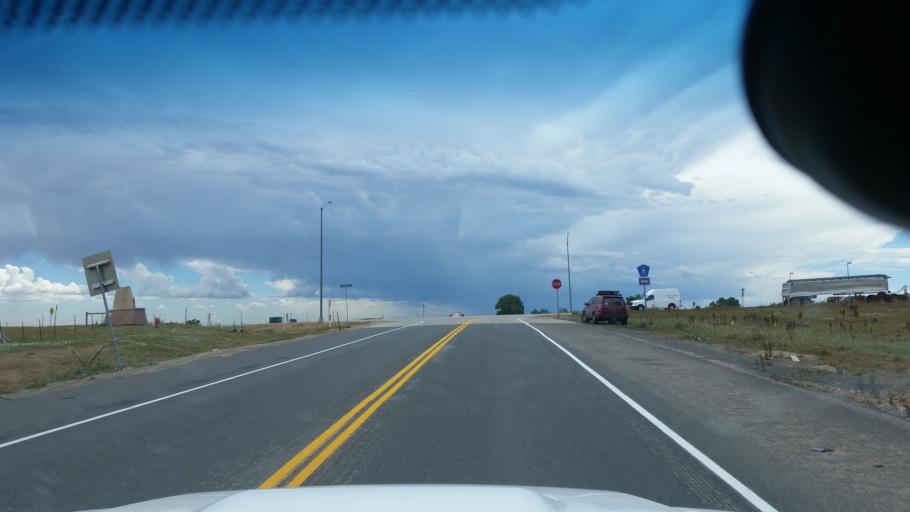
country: US
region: Colorado
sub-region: Weld County
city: Dacono
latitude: 40.0448
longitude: -104.9764
